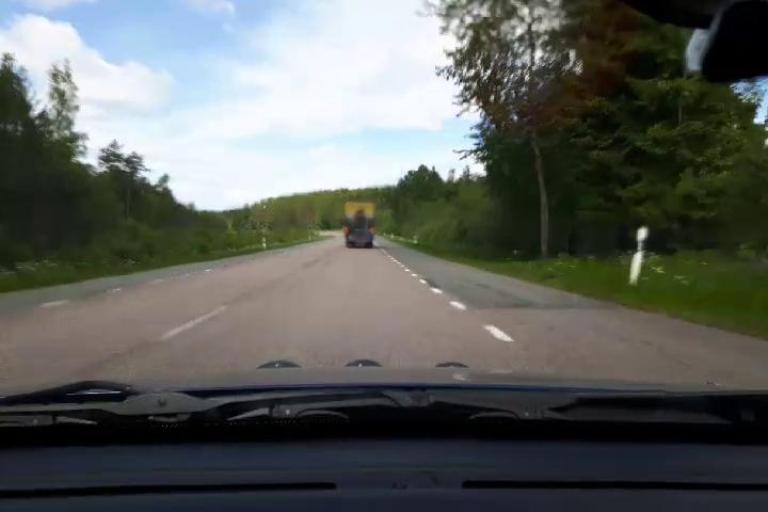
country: SE
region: Uppsala
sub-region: Osthammars Kommun
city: Bjorklinge
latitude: 60.0978
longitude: 17.5537
